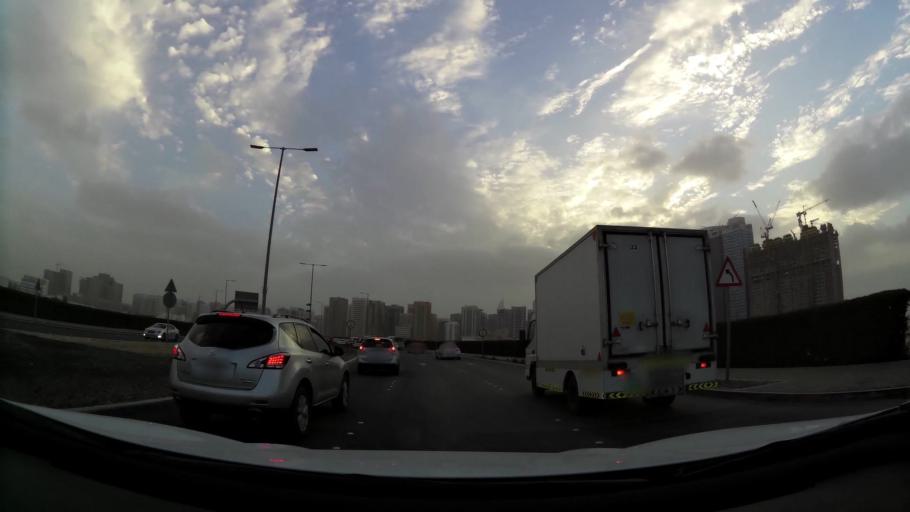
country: AE
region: Abu Dhabi
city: Abu Dhabi
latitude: 24.5084
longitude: 54.3814
